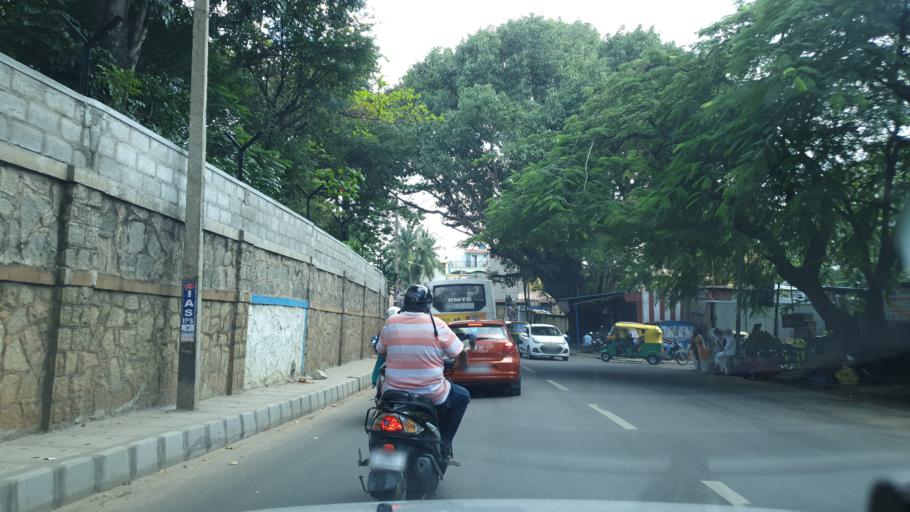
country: IN
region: Karnataka
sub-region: Bangalore Urban
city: Bangalore
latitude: 13.0266
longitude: 77.5618
